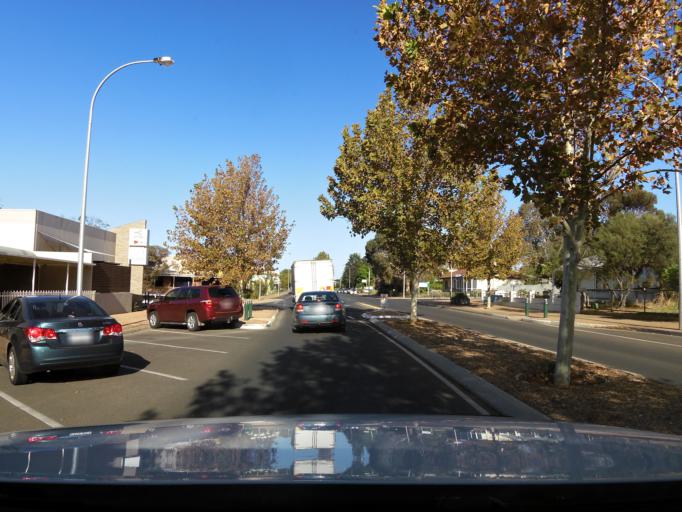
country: AU
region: South Australia
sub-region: Berri and Barmera
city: Berri
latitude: -34.2835
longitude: 140.6044
